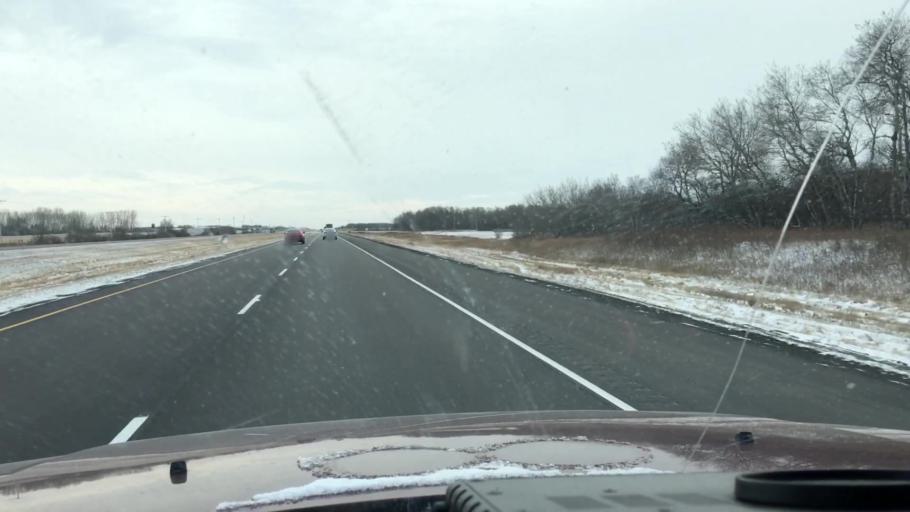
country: CA
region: Saskatchewan
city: Saskatoon
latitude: 51.9758
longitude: -106.5568
